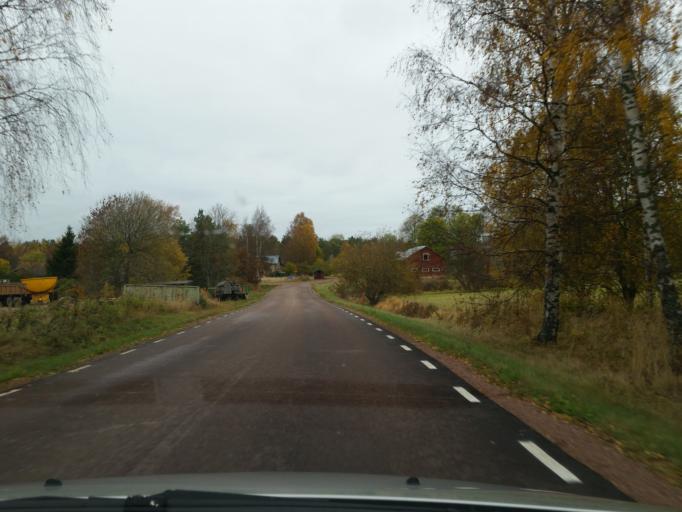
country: AX
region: Alands landsbygd
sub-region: Lemland
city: Lemland
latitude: 60.0772
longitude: 20.0830
